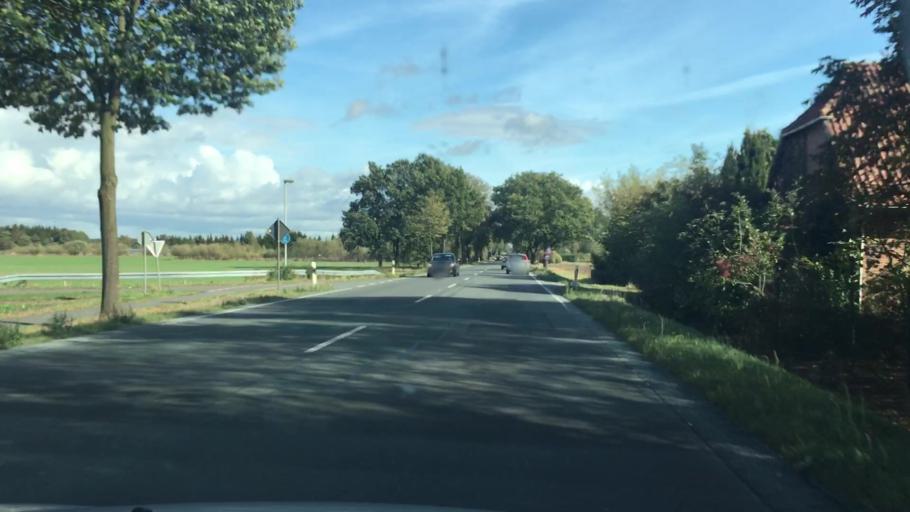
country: DE
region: Lower Saxony
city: Borstel
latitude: 52.6672
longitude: 8.9901
